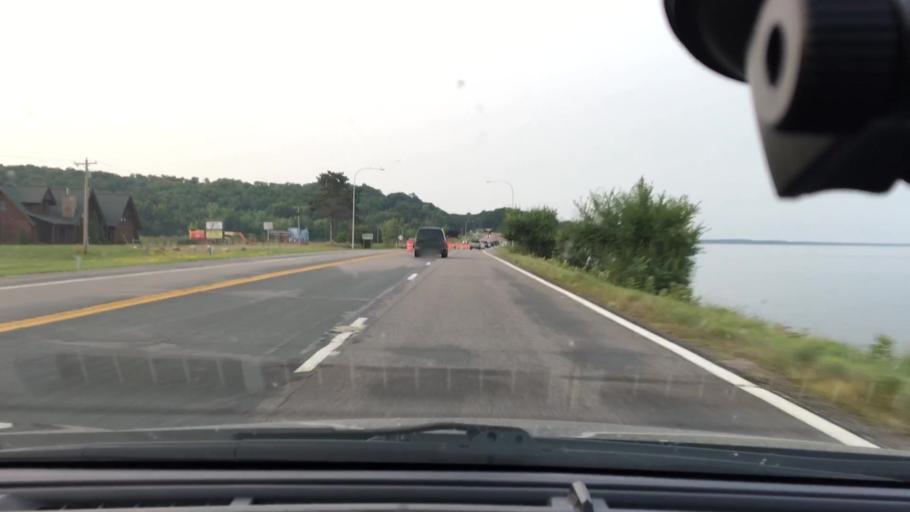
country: US
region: Minnesota
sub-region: Mille Lacs County
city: Vineland
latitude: 46.2726
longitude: -93.8227
